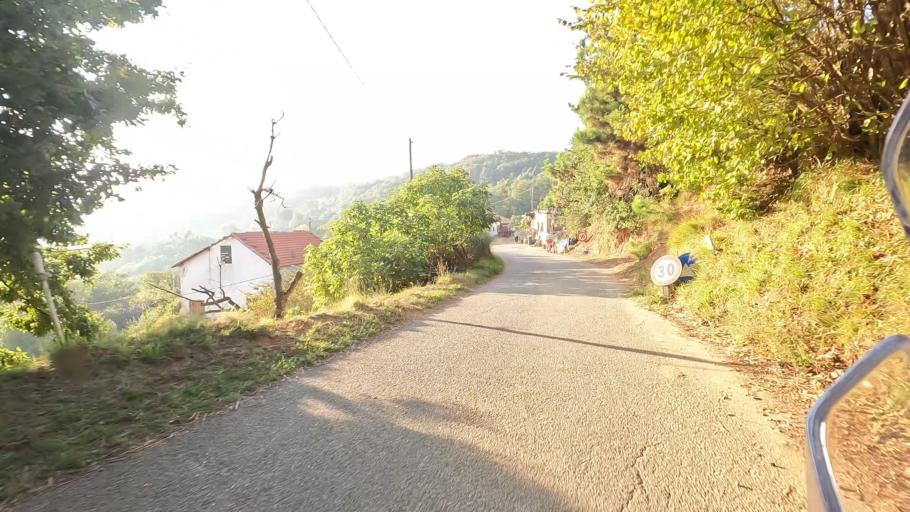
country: IT
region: Liguria
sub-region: Provincia di Savona
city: San Giovanni
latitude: 44.3934
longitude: 8.5283
